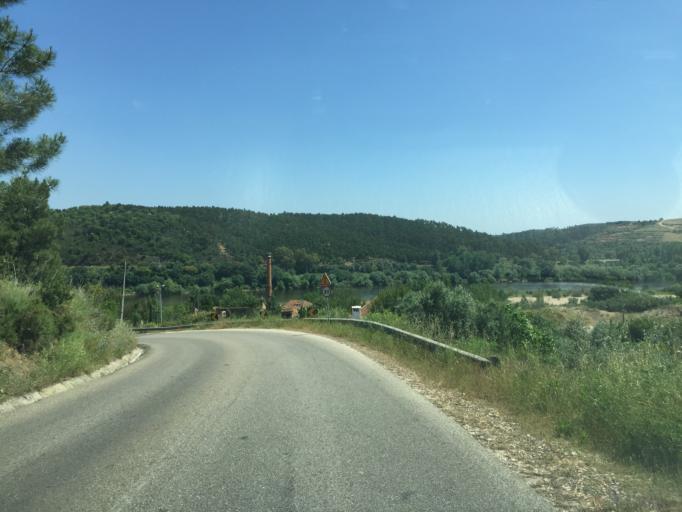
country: PT
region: Santarem
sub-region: Constancia
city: Constancia
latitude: 39.4688
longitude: -8.3465
